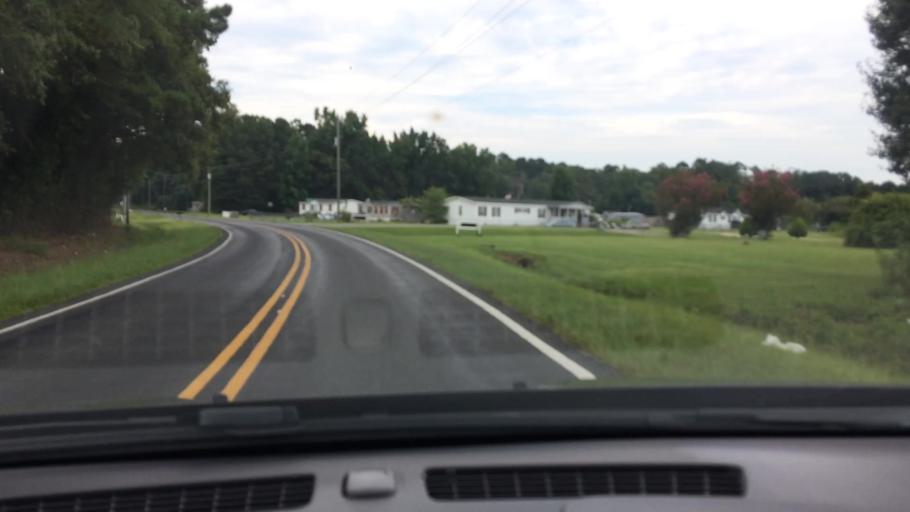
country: US
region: North Carolina
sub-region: Pitt County
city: Ayden
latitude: 35.4358
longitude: -77.4073
